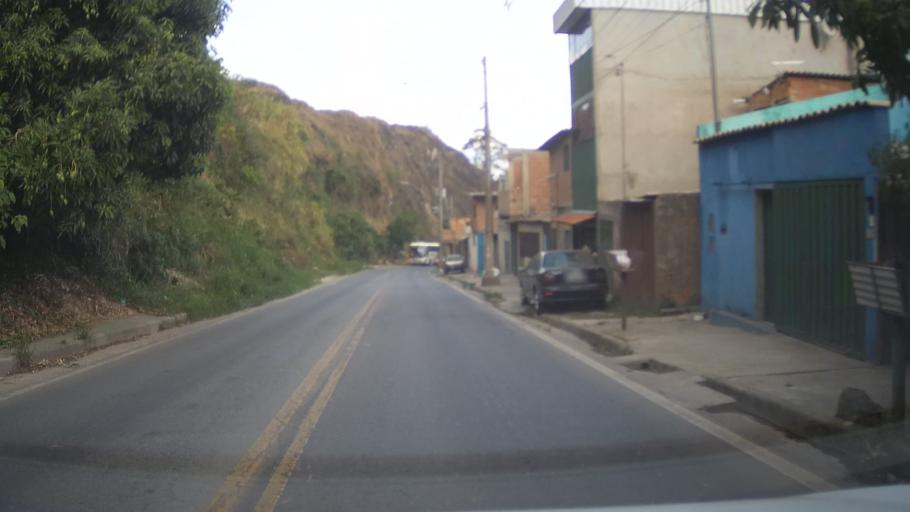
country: BR
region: Minas Gerais
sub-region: Belo Horizonte
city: Belo Horizonte
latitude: -19.8644
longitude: -43.8922
